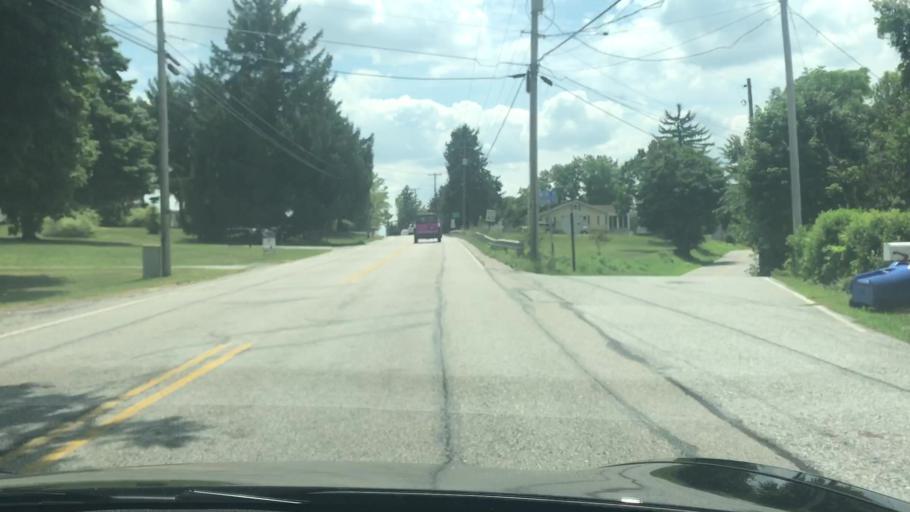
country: US
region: Pennsylvania
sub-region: York County
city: Manchester
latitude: 40.0563
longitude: -76.7660
